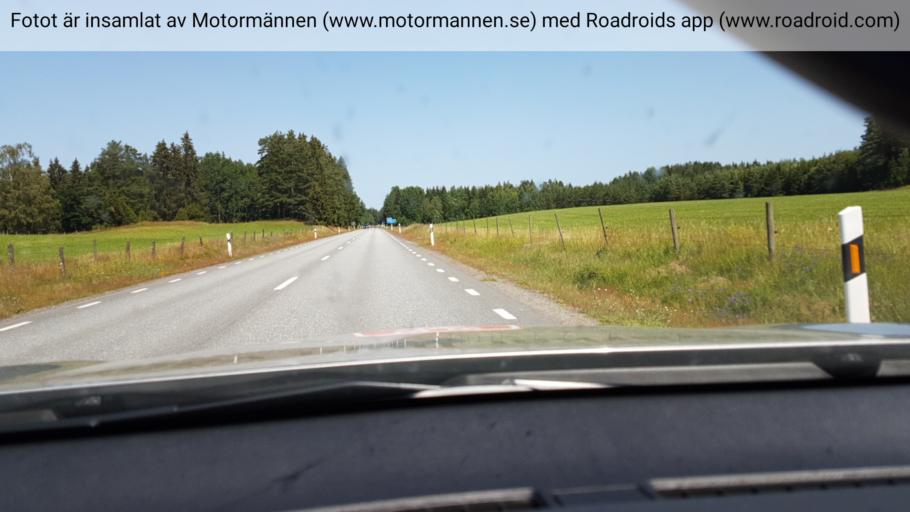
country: SE
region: Joenkoeping
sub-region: Savsjo Kommun
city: Saevsjoe
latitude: 57.4235
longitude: 14.6935
